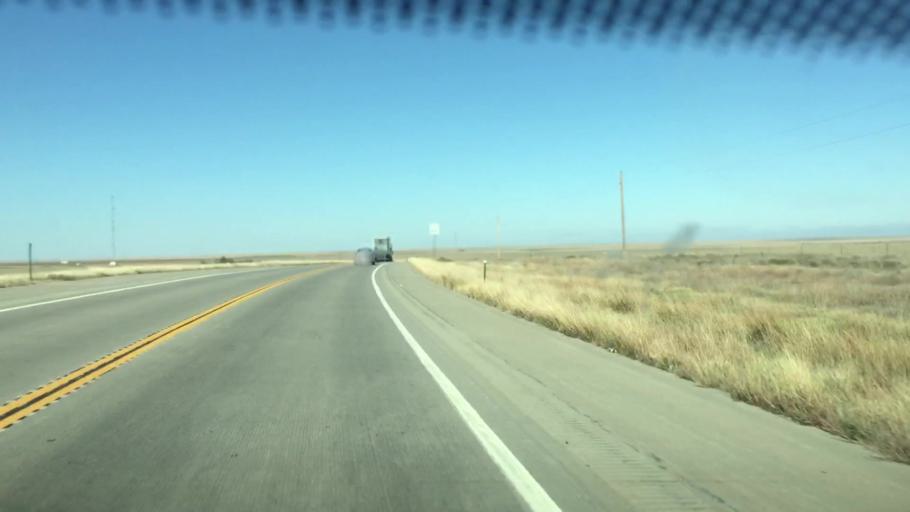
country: US
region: Colorado
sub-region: Prowers County
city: Lamar
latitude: 38.2697
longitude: -102.7227
